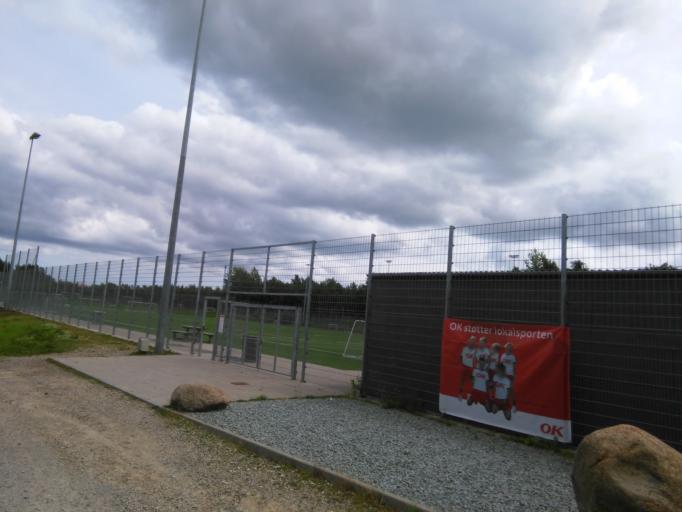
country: DK
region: Central Jutland
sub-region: Arhus Kommune
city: Arhus
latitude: 56.1109
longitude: 10.1929
